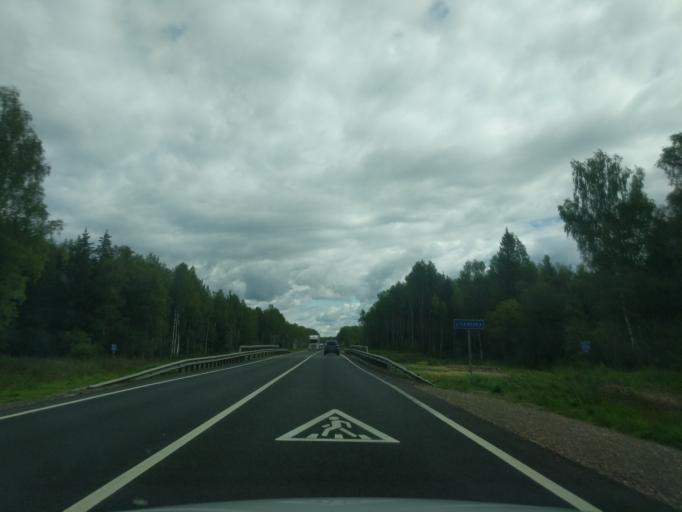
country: RU
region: Jaroslavl
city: Tunoshna
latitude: 57.5600
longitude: 40.2302
